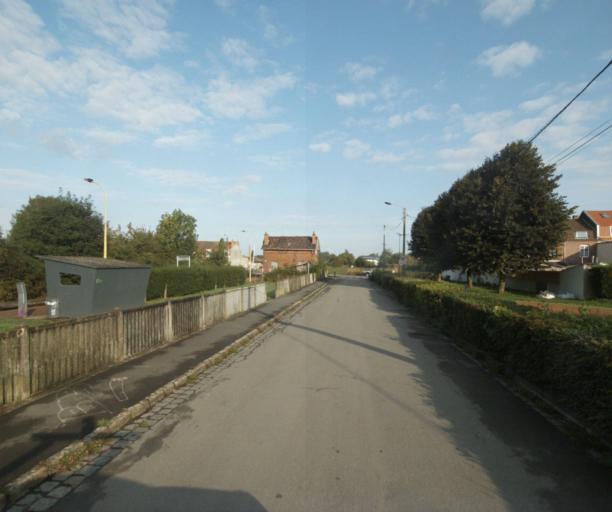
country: FR
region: Nord-Pas-de-Calais
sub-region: Departement du Nord
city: Wambrechies
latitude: 50.6812
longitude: 3.0407
